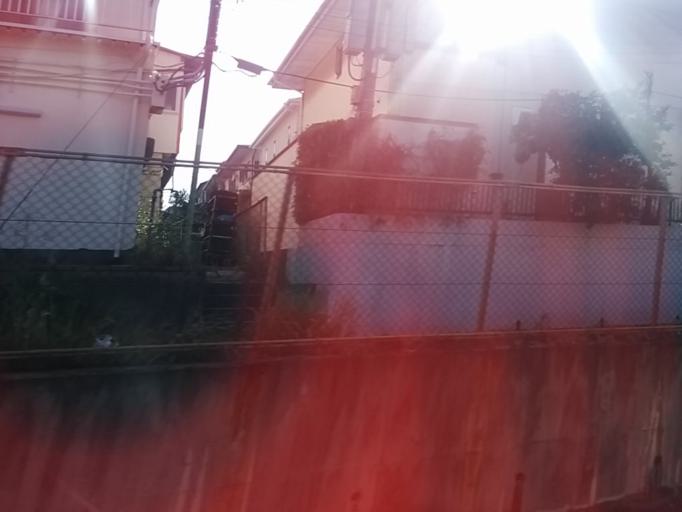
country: JP
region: Nara
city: Nara-shi
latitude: 34.7154
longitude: 135.7921
